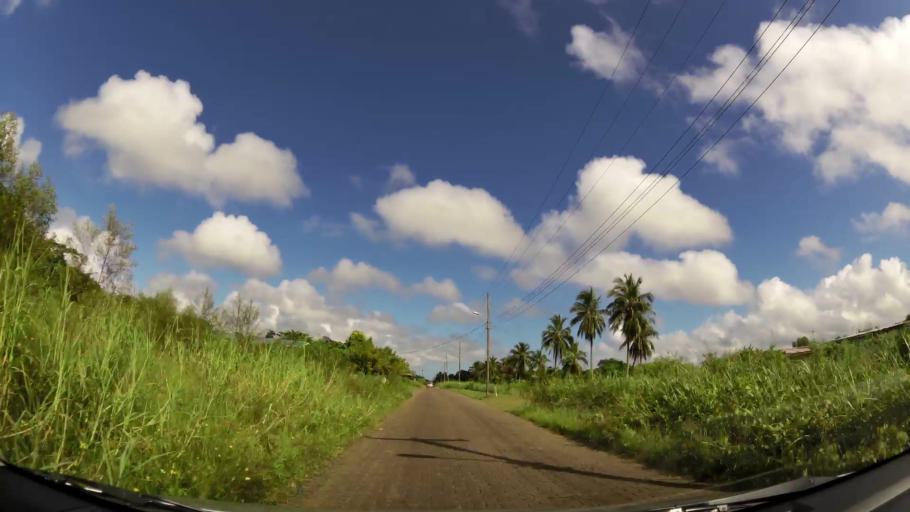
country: SR
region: Commewijne
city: Nieuw Amsterdam
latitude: 5.8742
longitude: -55.1036
